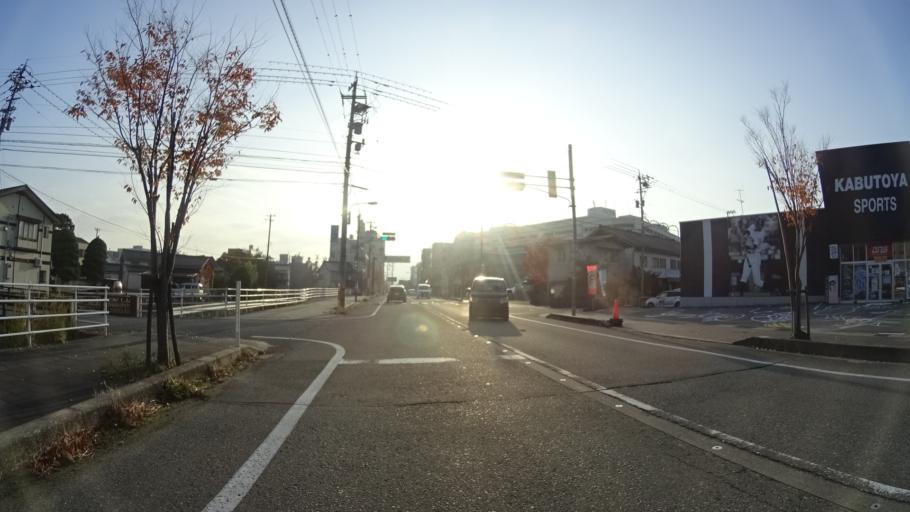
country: JP
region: Ishikawa
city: Nanao
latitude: 37.0447
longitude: 136.9617
